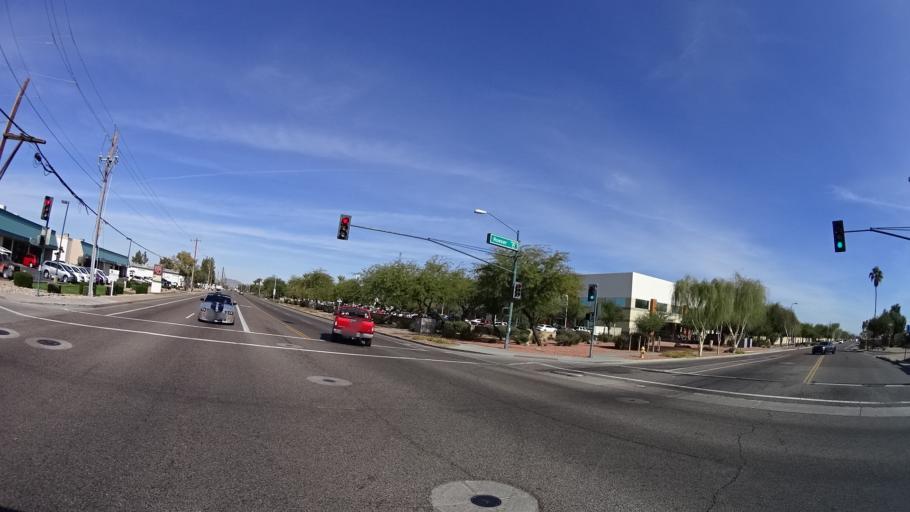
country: US
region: Arizona
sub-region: Maricopa County
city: Guadalupe
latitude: 33.4000
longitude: -111.9956
